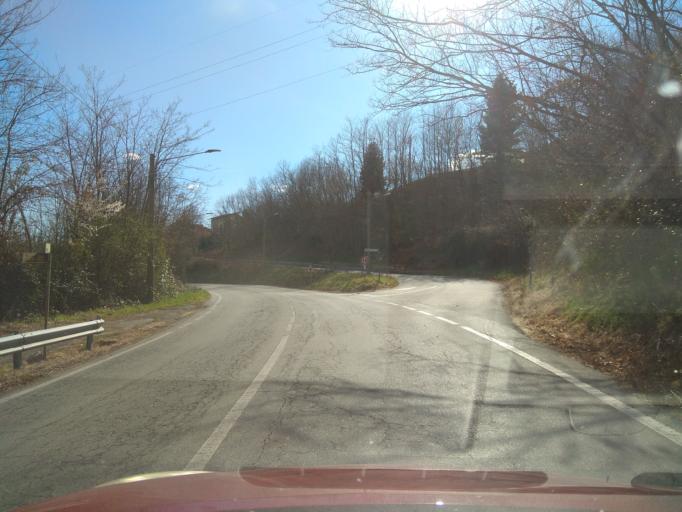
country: IT
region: Piedmont
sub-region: Provincia di Biella
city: Lessona
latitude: 45.5943
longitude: 8.1831
